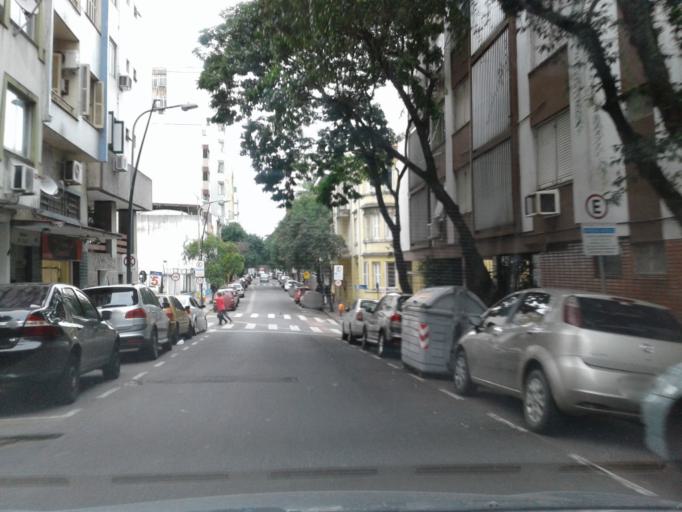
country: BR
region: Rio Grande do Sul
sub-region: Porto Alegre
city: Porto Alegre
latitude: -30.0322
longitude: -51.2327
